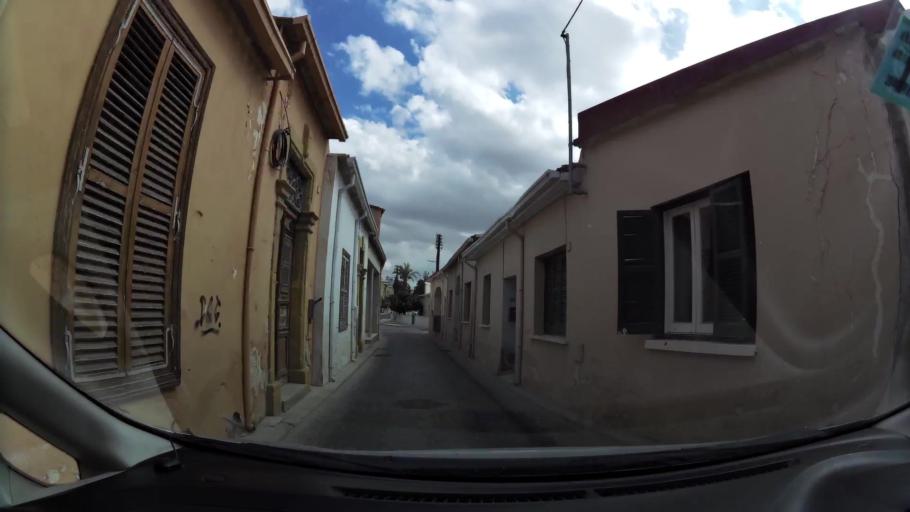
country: CY
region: Lefkosia
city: Nicosia
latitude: 35.1741
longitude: 33.3801
